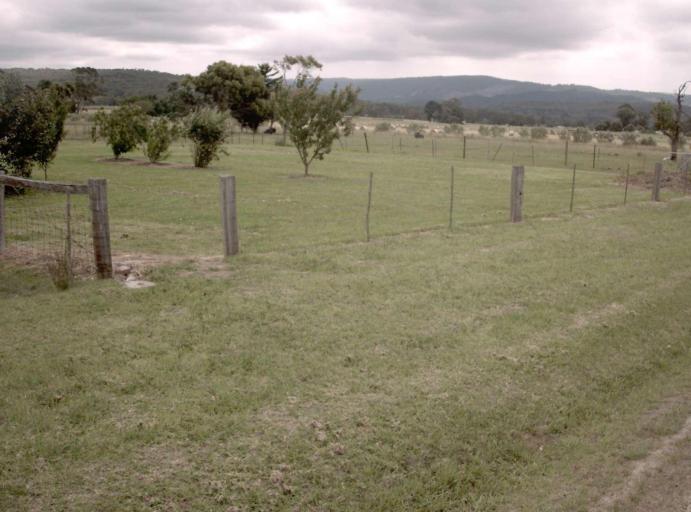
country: AU
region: Victoria
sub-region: Latrobe
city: Traralgon
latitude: -38.5181
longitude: 146.6613
